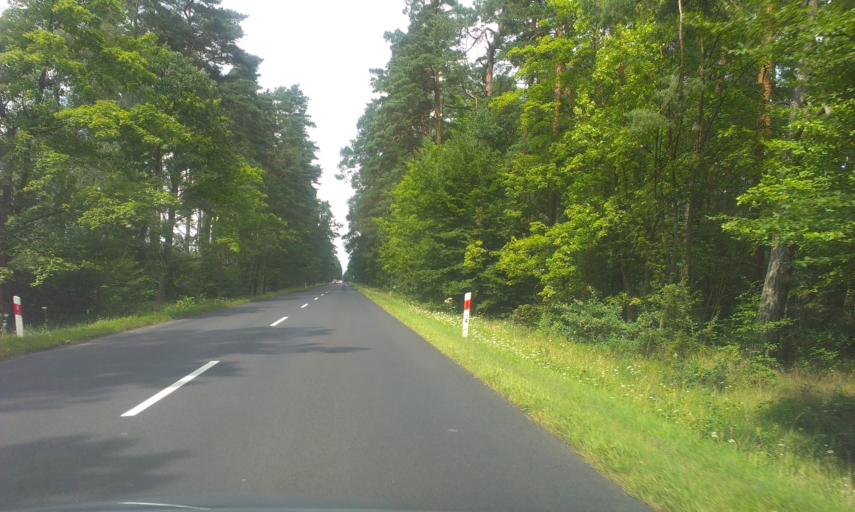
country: PL
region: West Pomeranian Voivodeship
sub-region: Powiat bialogardzki
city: Bialogard
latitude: 53.9605
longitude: 16.0539
